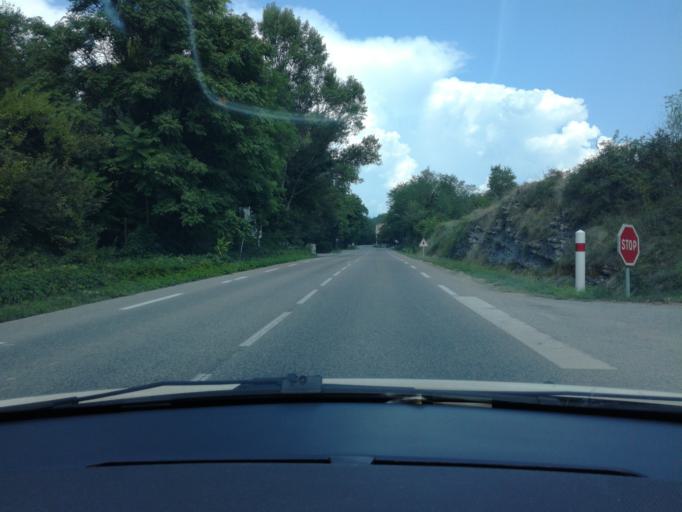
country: FR
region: Rhone-Alpes
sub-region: Departement de l'Ardeche
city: Ruoms
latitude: 44.4850
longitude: 4.3805
